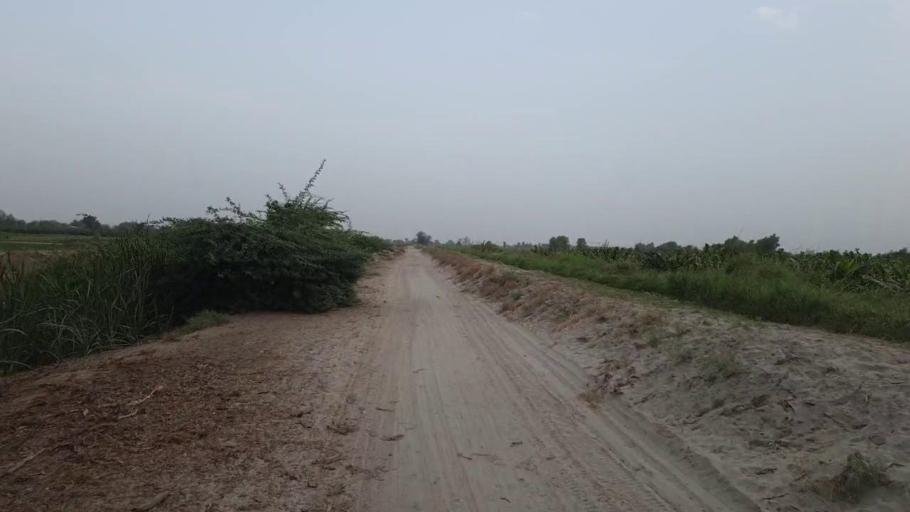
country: PK
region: Sindh
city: Daur
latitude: 26.4136
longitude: 68.2252
